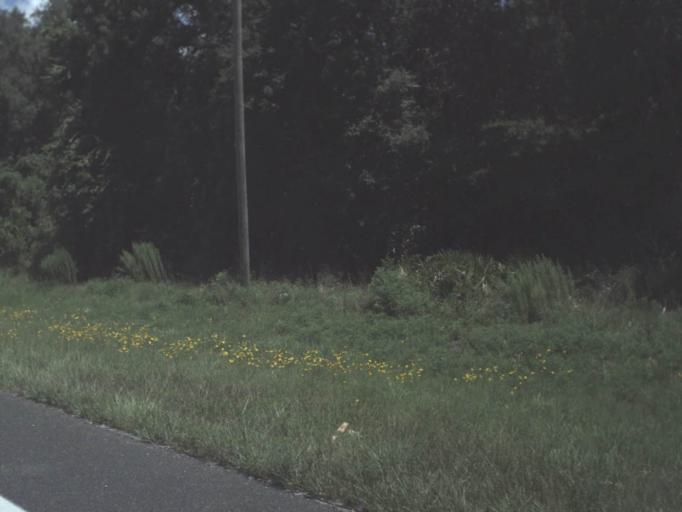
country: US
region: Florida
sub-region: Levy County
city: Manatee Road
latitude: 29.5641
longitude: -82.9084
